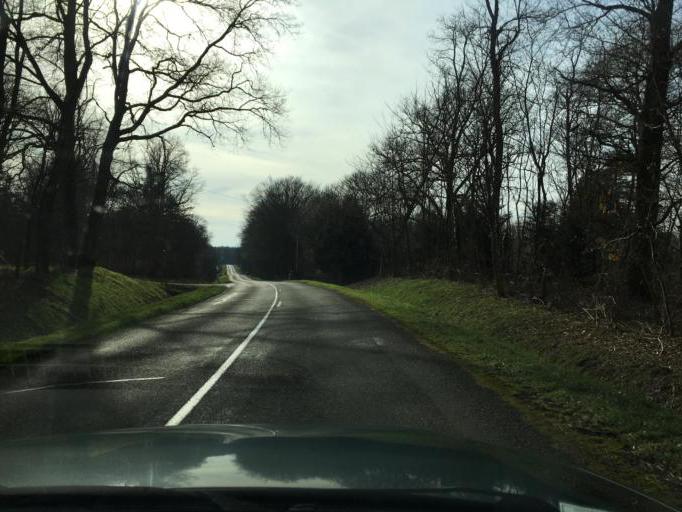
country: FR
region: Centre
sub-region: Departement du Loiret
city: Jouy-le-Potier
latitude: 47.7043
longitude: 1.8420
